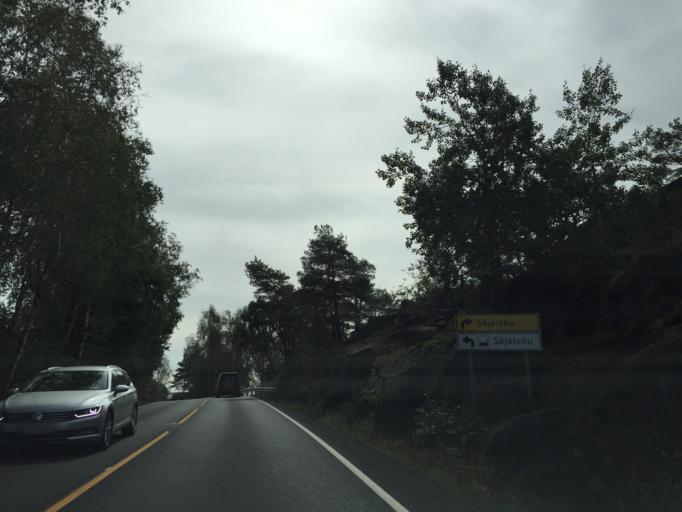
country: NO
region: Ostfold
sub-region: Fredrikstad
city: Fredrikstad
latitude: 59.0990
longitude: 10.9073
